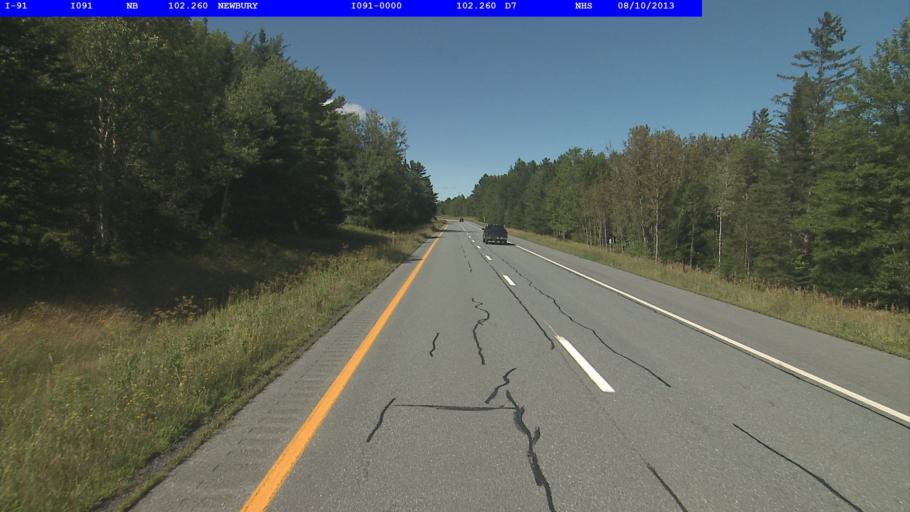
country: US
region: New Hampshire
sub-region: Grafton County
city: Haverhill
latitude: 44.0461
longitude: -72.1072
